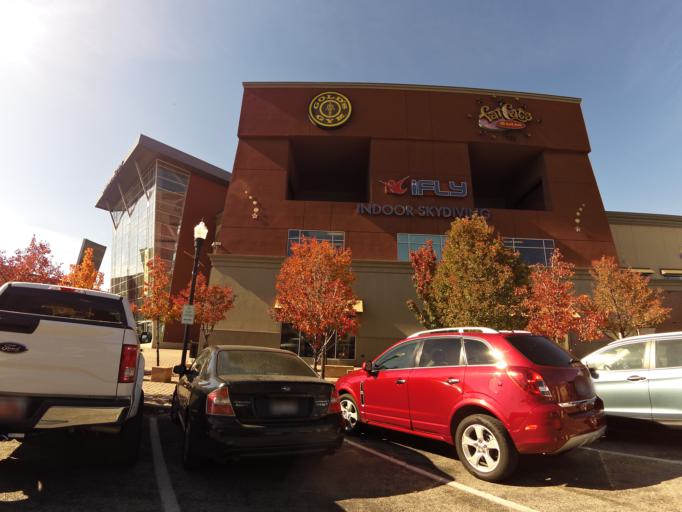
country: US
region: Utah
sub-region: Weber County
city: Ogden
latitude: 41.2253
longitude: -111.9715
